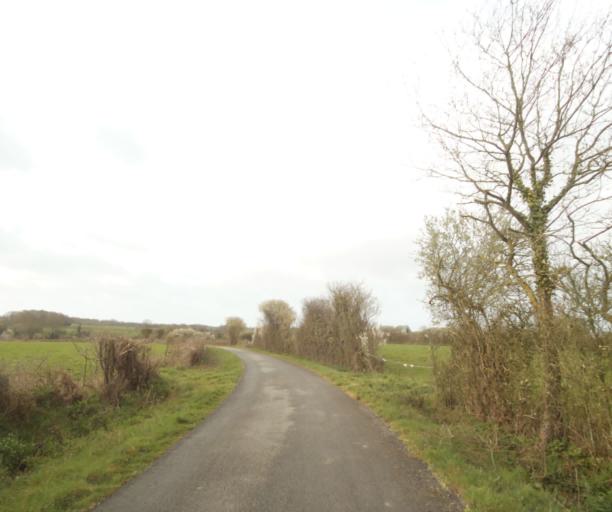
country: FR
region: Pays de la Loire
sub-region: Departement de la Loire-Atlantique
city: Bouvron
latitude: 47.4076
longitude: -1.8747
